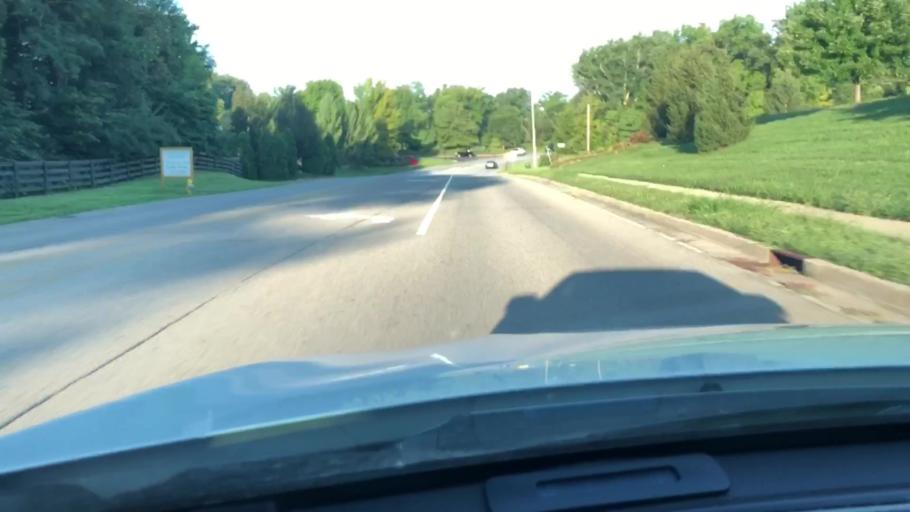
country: US
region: Kentucky
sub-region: Jefferson County
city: Middletown
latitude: 38.2168
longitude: -85.5302
